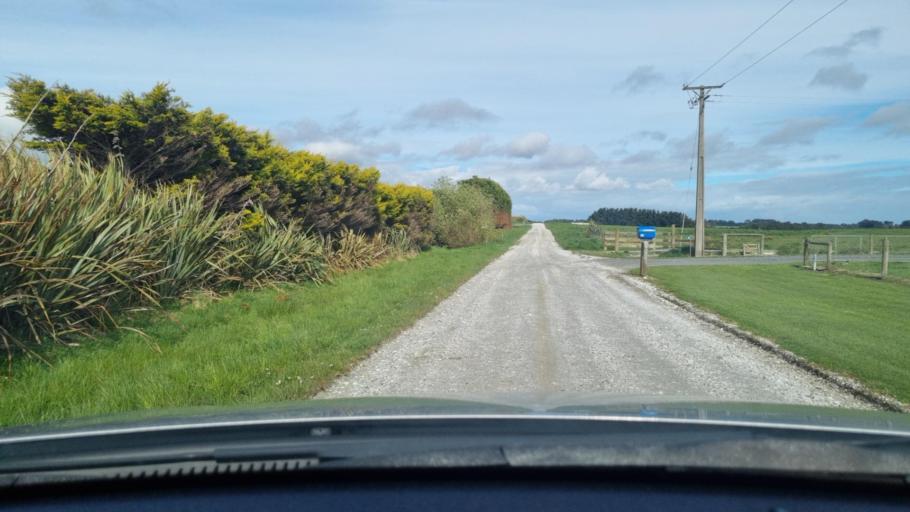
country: NZ
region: Southland
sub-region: Invercargill City
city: Invercargill
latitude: -46.4540
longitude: 168.3839
